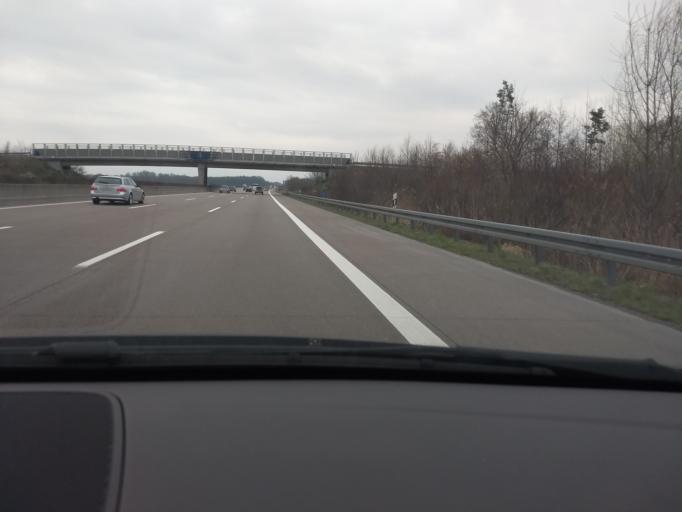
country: DE
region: Baden-Wuerttemberg
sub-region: Freiburg Region
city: Renchen
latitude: 48.5802
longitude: 7.9692
